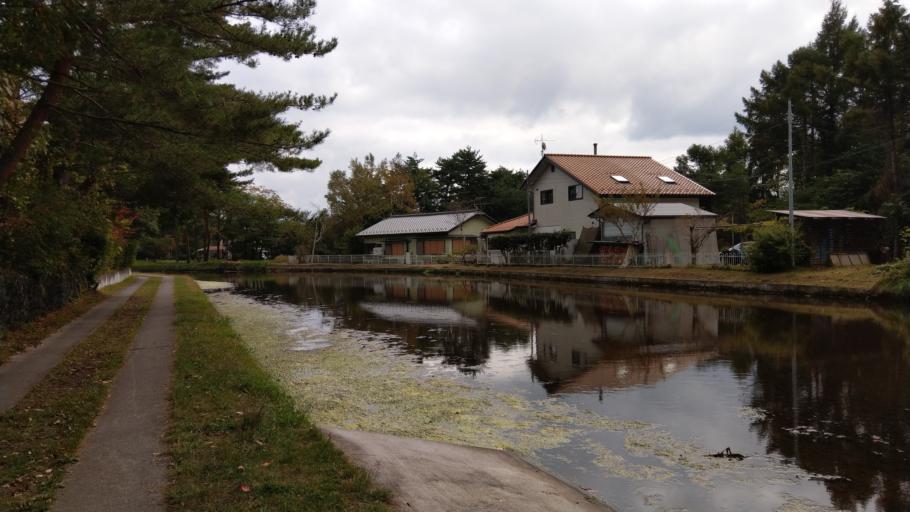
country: JP
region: Nagano
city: Komoro
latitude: 36.3298
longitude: 138.5281
